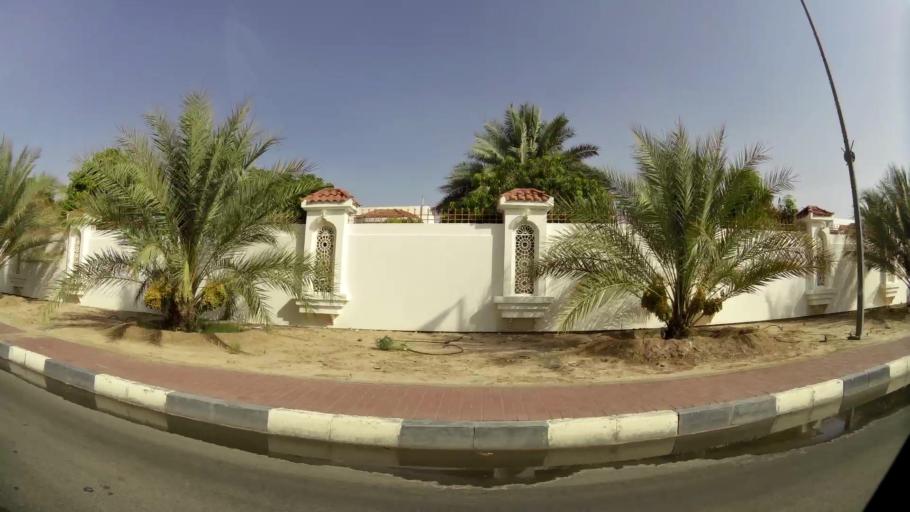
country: AE
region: Abu Dhabi
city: Al Ain
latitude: 24.2326
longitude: 55.6697
